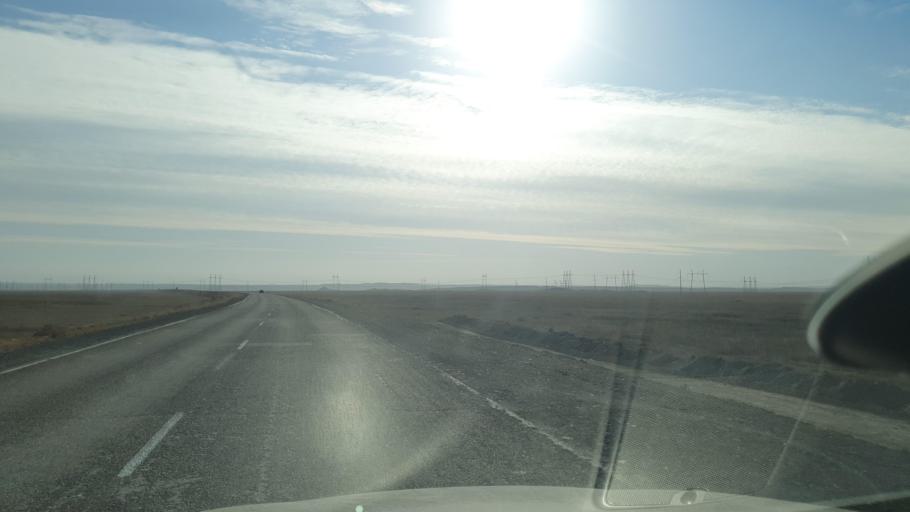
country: KZ
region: Zhambyl
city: Mynaral
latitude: 45.6147
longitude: 73.3957
